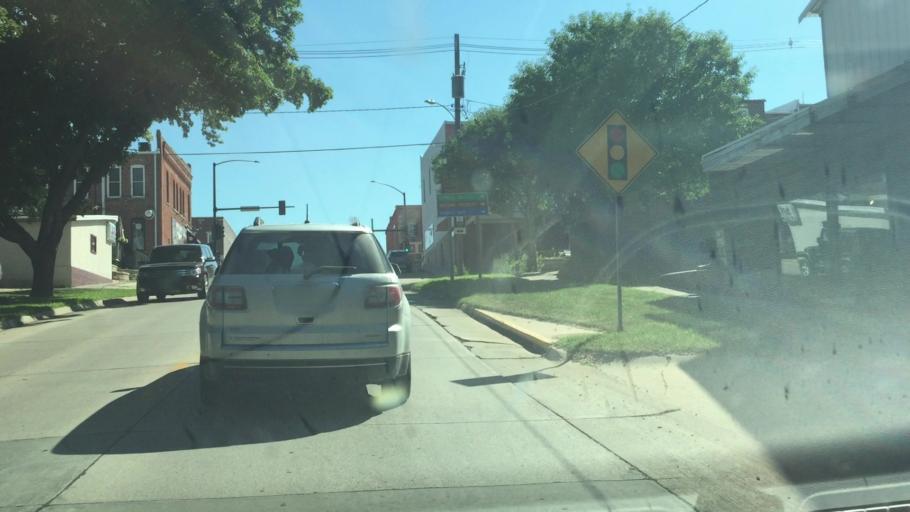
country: US
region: Iowa
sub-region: Linn County
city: Mount Vernon
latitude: 41.9230
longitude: -91.4164
